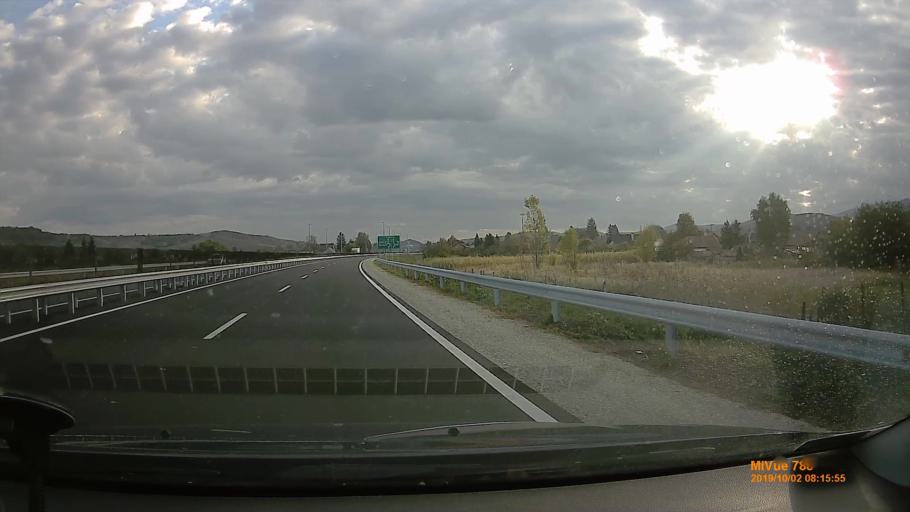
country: HU
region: Nograd
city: Matraverebely
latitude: 47.9731
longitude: 19.7724
